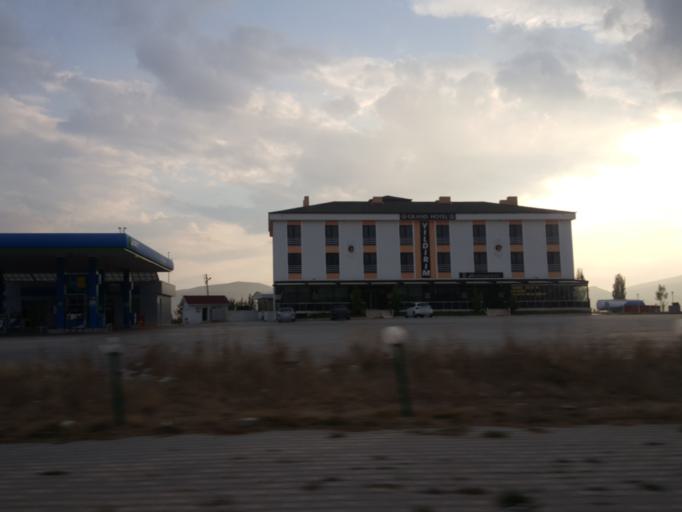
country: TR
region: Amasya
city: Gumushacikoy
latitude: 40.8748
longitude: 35.2375
